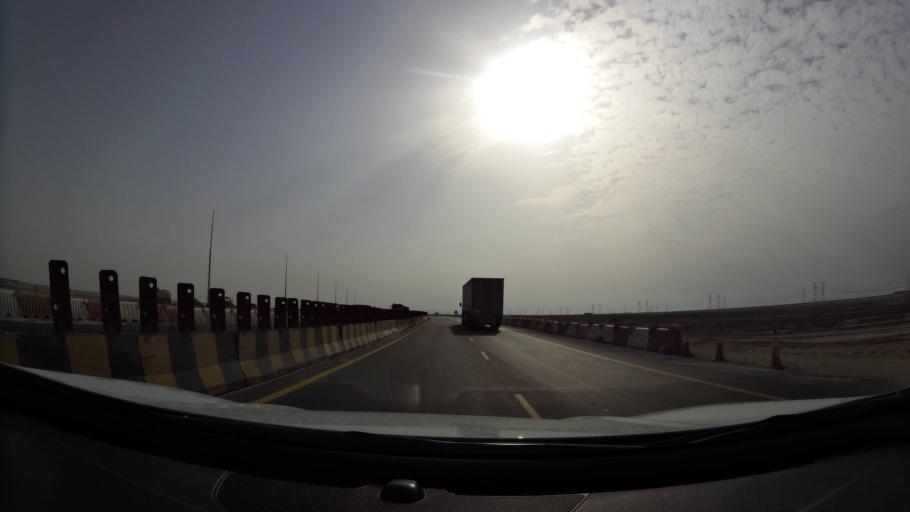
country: AE
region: Abu Dhabi
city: Abu Dhabi
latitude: 24.2438
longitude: 54.4696
